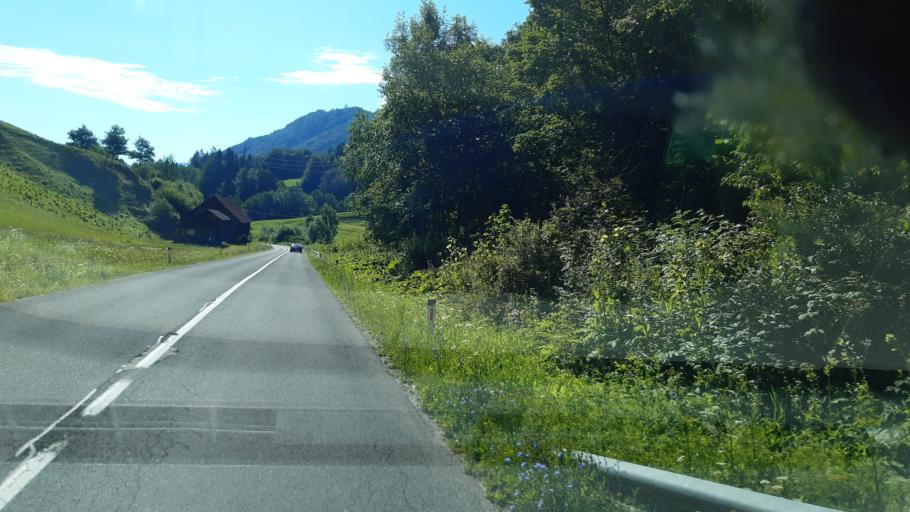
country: SI
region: Gornji Grad
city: Gornji Grad
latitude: 46.2152
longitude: 14.8229
